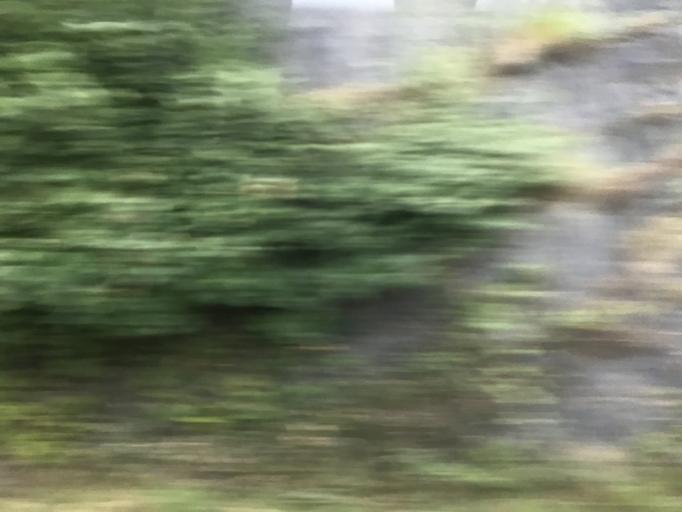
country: ES
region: Basque Country
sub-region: Provincia de Guipuzcoa
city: Isasondo
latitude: 43.0765
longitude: -2.1583
